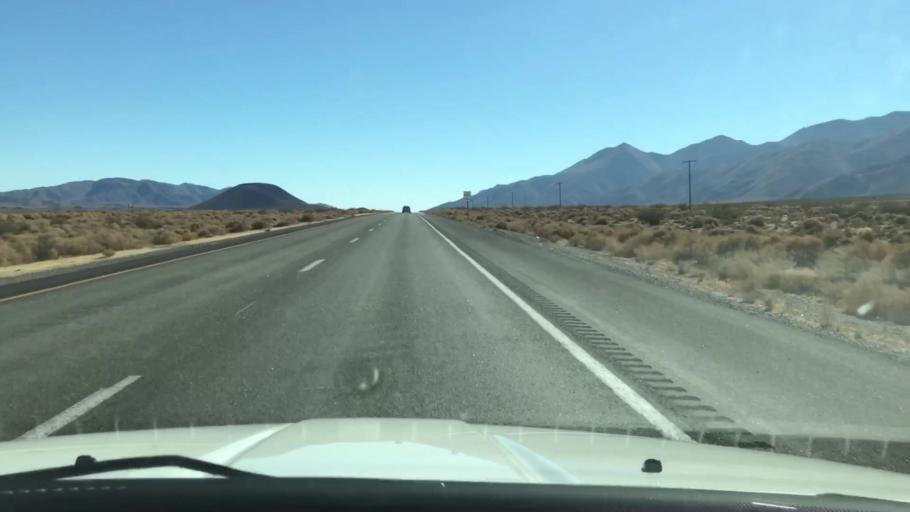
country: US
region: California
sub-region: Kern County
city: Inyokern
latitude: 36.0343
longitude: -117.9444
